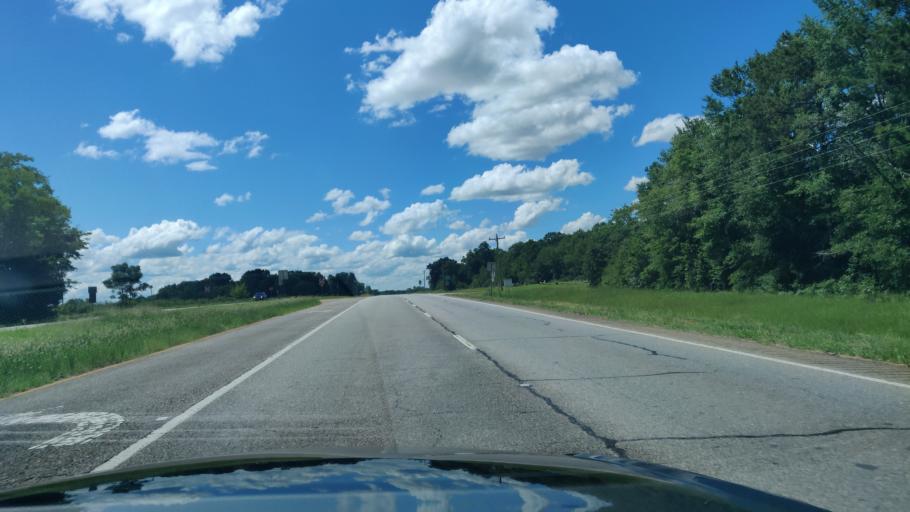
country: US
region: Georgia
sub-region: Stewart County
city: Richland
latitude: 32.0097
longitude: -84.6542
